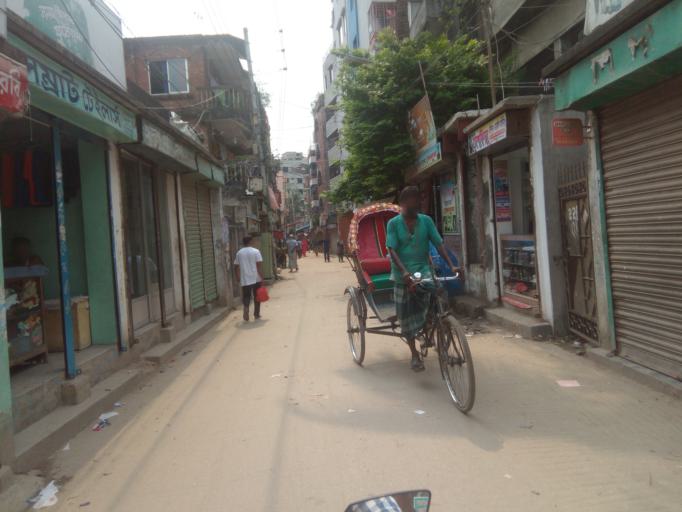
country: BD
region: Dhaka
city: Paltan
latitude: 23.7609
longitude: 90.4239
